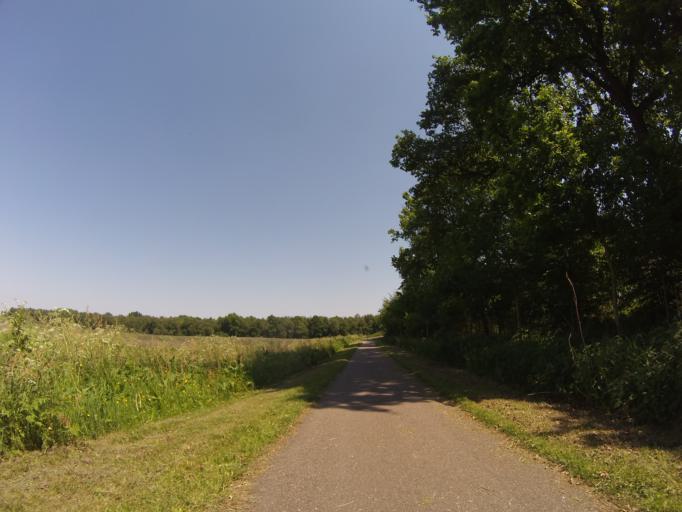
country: NL
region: Drenthe
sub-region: Gemeente Coevorden
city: Sleen
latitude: 52.7104
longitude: 6.8294
